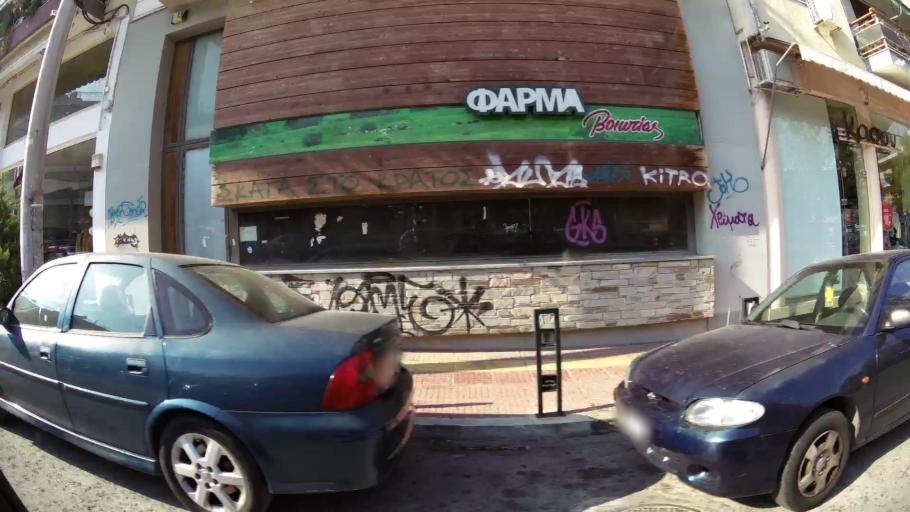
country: GR
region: Attica
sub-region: Nomarchia Athinas
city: Galatsi
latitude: 38.0217
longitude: 23.7510
